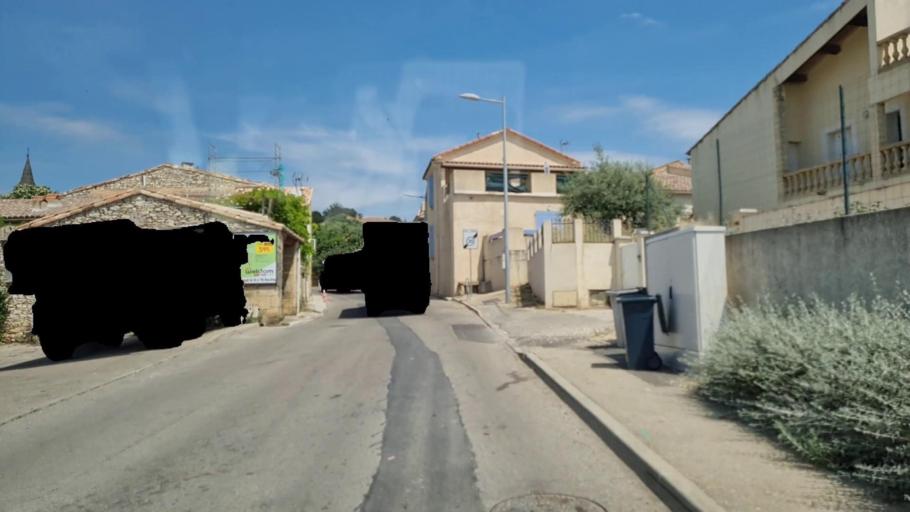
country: FR
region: Languedoc-Roussillon
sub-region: Departement du Gard
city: Cabrieres
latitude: 43.9032
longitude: 4.4735
